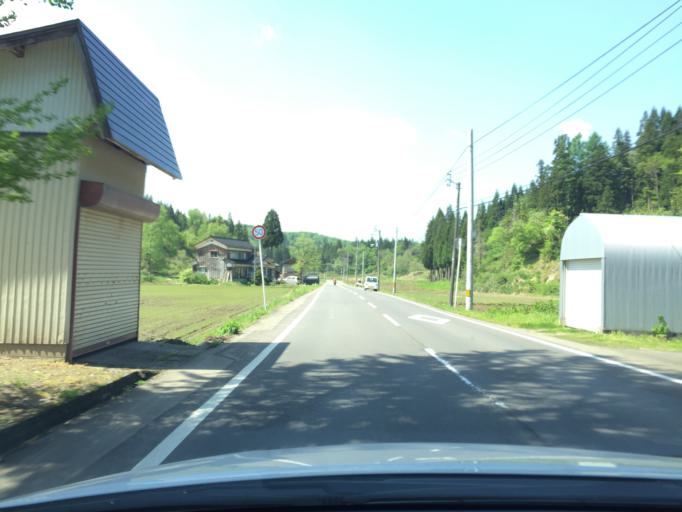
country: JP
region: Niigata
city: Tochio-honcho
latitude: 37.5089
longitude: 139.0743
